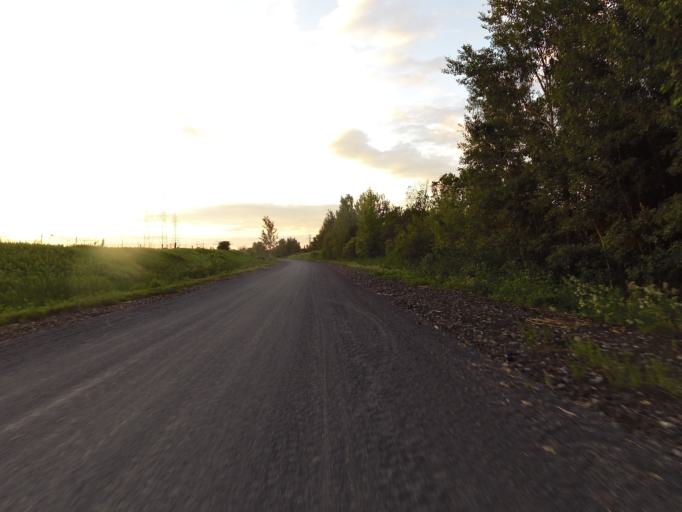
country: CA
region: Ontario
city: Arnprior
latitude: 45.3967
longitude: -76.3223
